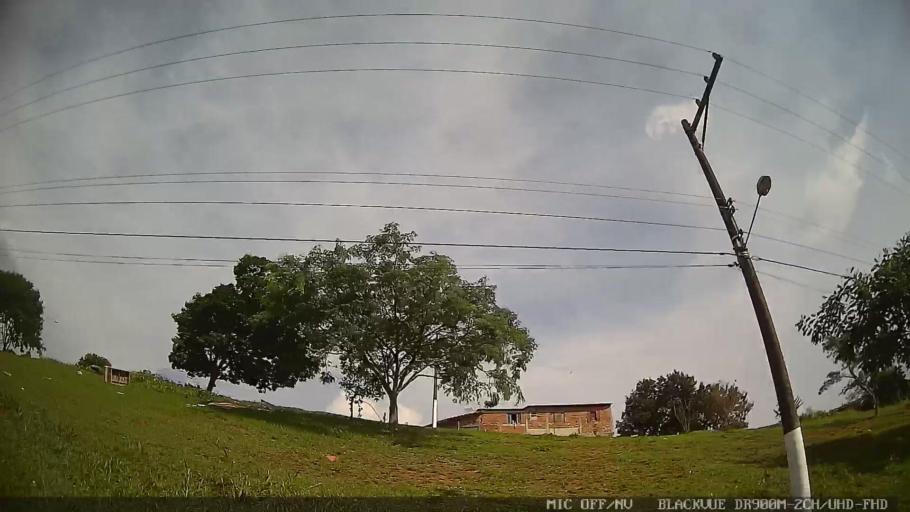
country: BR
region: Sao Paulo
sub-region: Braganca Paulista
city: Braganca Paulista
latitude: -22.9150
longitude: -46.5463
